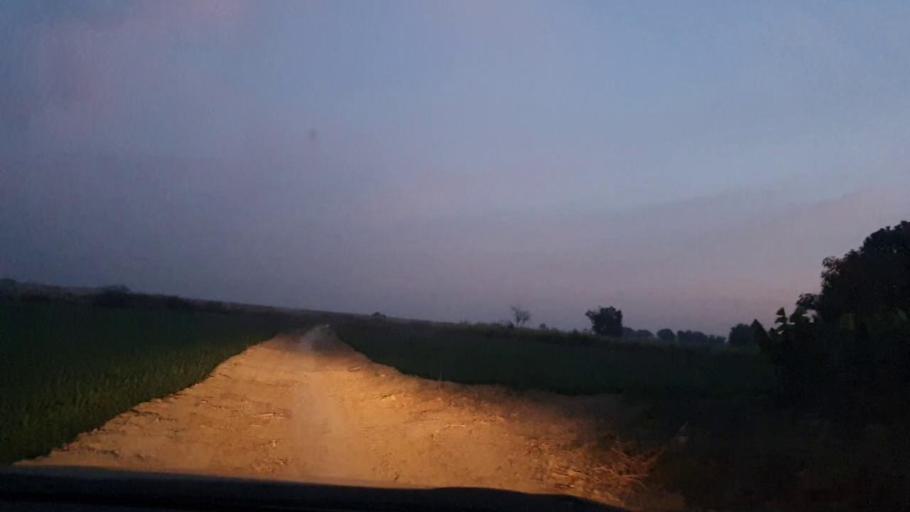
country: PK
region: Sindh
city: Sakrand
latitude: 26.1839
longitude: 68.3059
